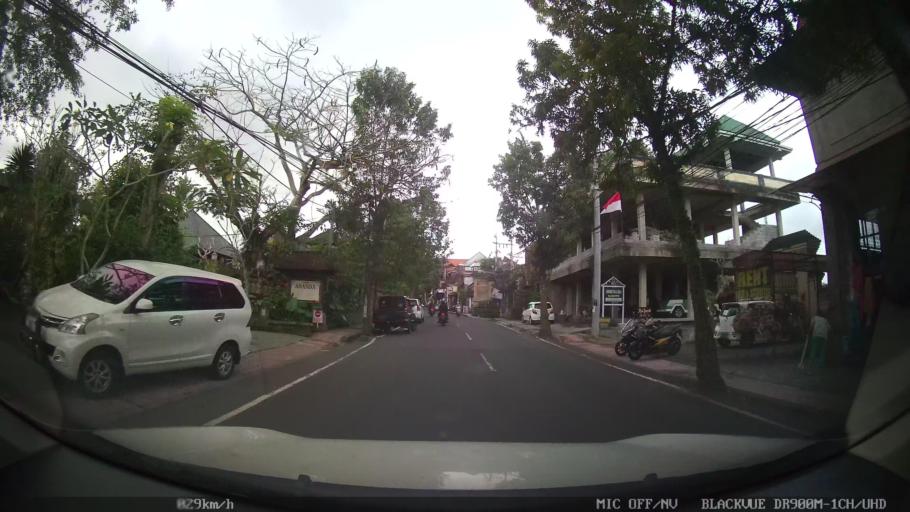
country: ID
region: Bali
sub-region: Kabupaten Gianyar
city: Ubud
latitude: -8.4967
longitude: 115.2535
